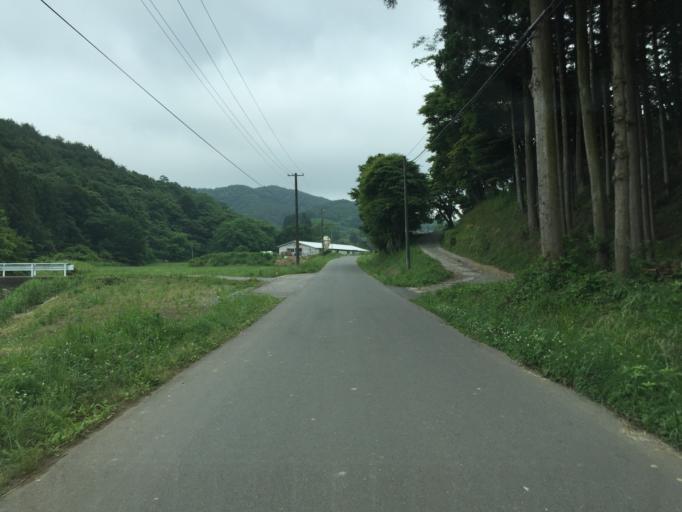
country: JP
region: Fukushima
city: Yanagawamachi-saiwaicho
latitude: 37.7859
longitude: 140.7168
